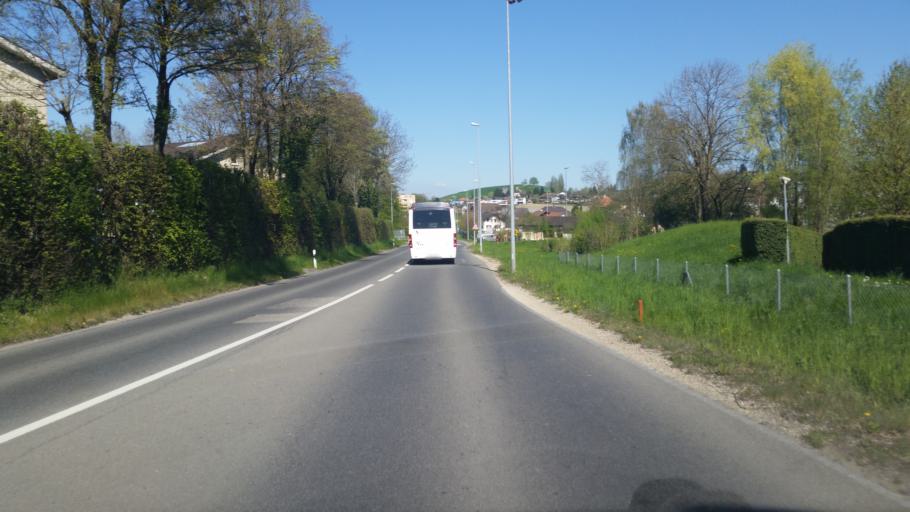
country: CH
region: Fribourg
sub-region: See District
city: Murten
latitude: 46.9372
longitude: 7.1407
